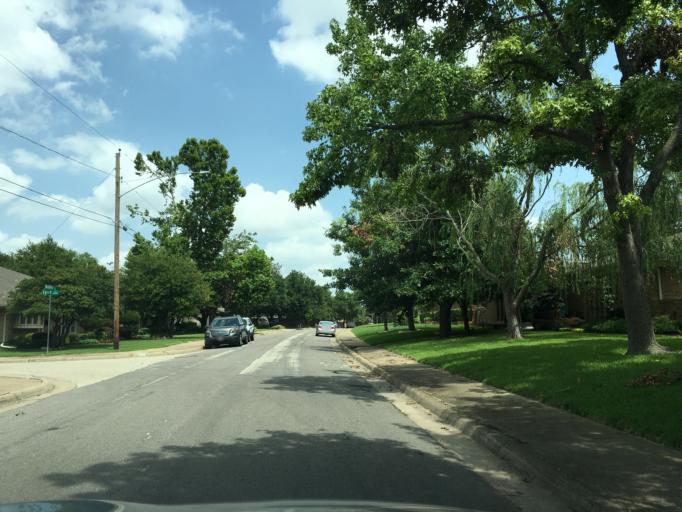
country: US
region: Texas
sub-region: Dallas County
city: University Park
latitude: 32.8899
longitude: -96.7804
